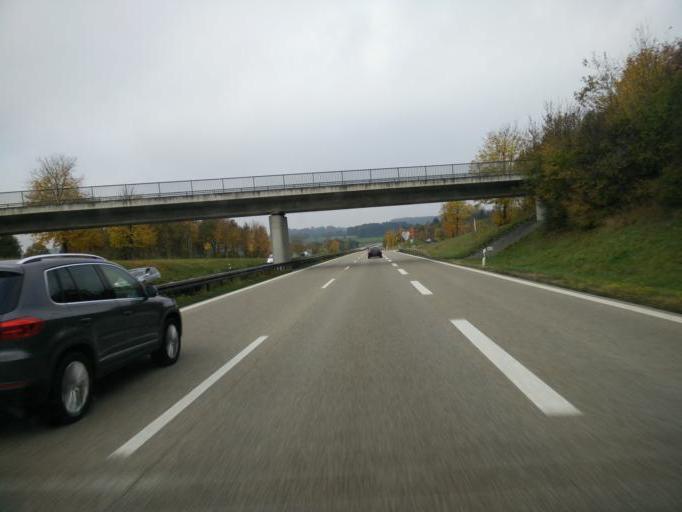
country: DE
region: Bavaria
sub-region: Swabia
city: Stetten
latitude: 48.0337
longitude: 10.4241
